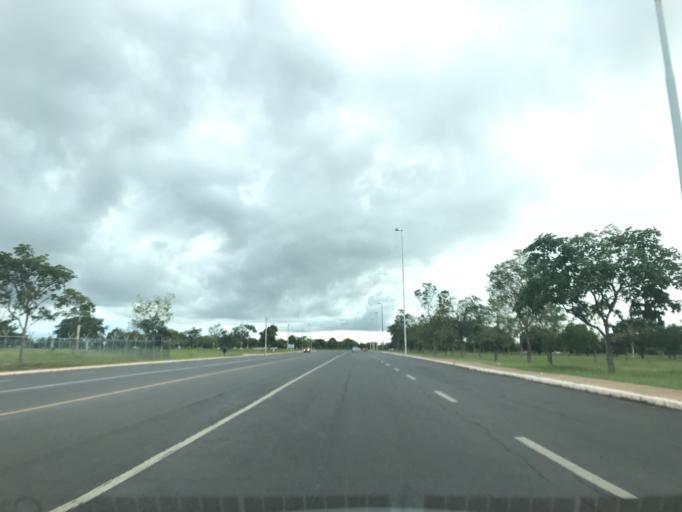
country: BR
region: Federal District
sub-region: Brasilia
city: Brasilia
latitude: -15.7774
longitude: -47.9215
